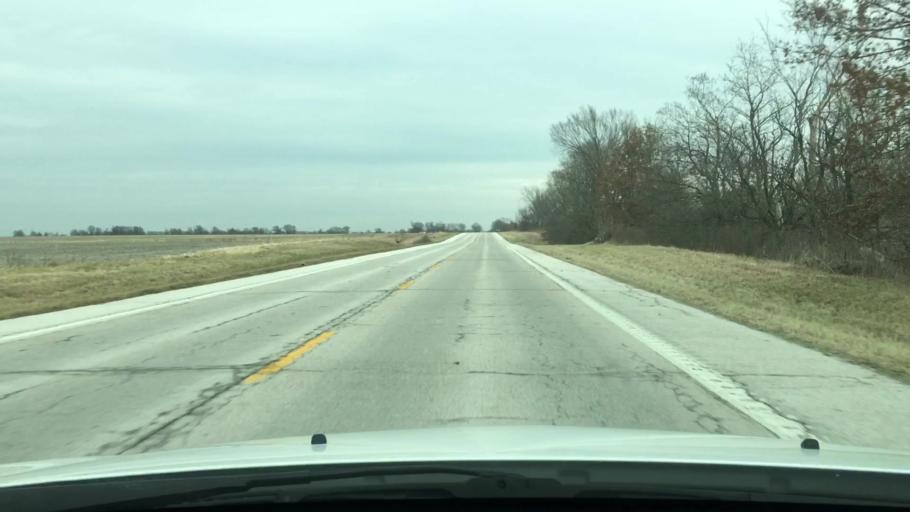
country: US
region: Missouri
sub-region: Audrain County
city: Vandalia
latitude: 39.3274
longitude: -91.4457
